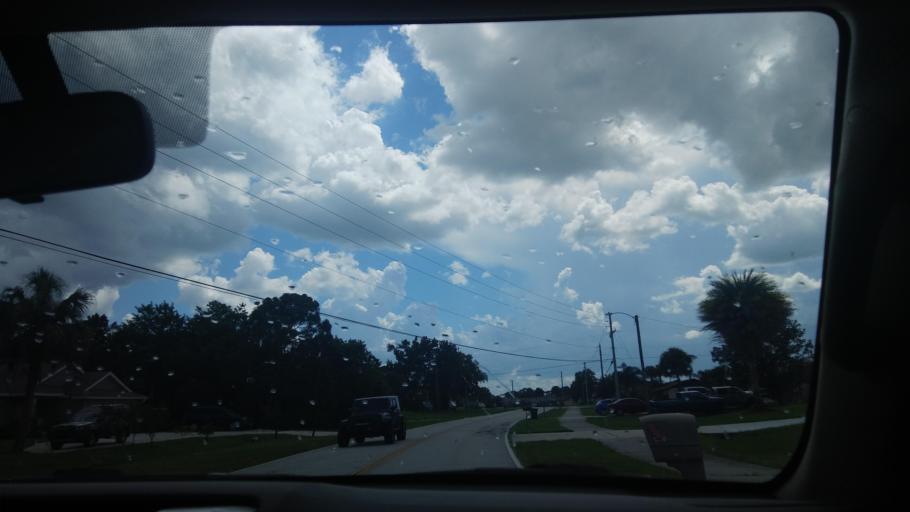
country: US
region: Florida
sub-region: Brevard County
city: Palm Bay
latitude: 28.0043
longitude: -80.6463
